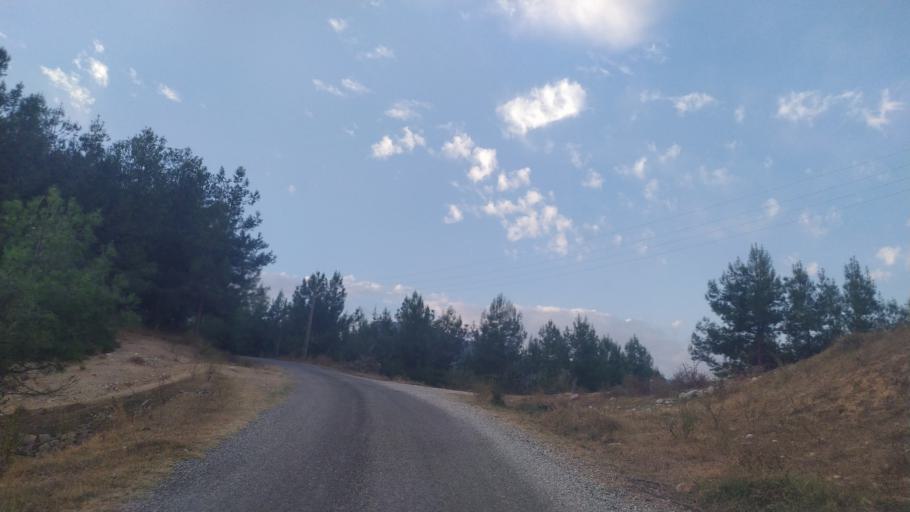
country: TR
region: Mersin
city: Camliyayla
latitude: 37.2249
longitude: 34.7108
